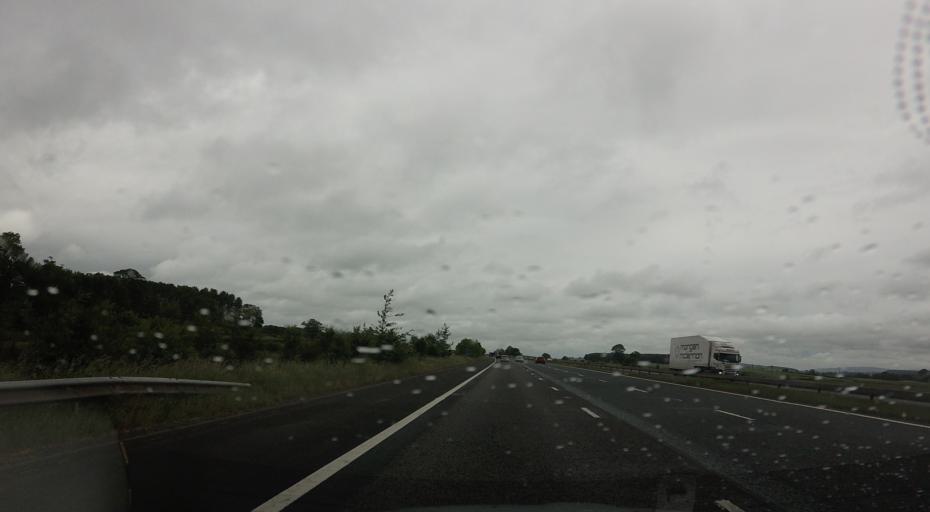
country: GB
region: England
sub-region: Cumbria
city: Penrith
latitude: 54.7273
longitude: -2.8020
